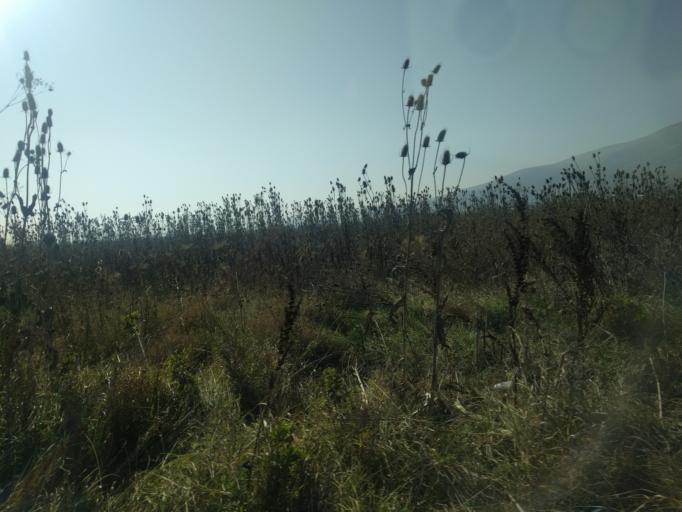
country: XK
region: Pristina
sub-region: Komuna e Gracanices
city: Glanica
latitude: 42.5868
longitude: 21.0187
